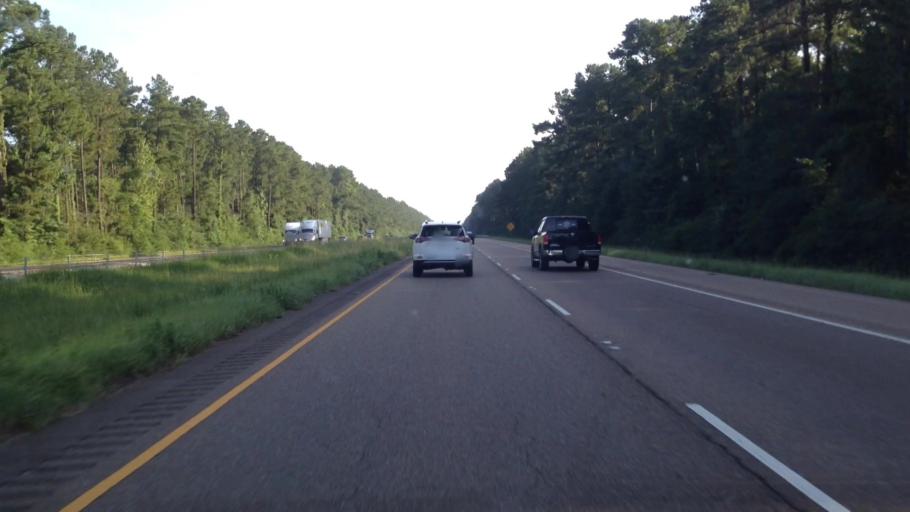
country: US
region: Louisiana
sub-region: Tangipahoa Parish
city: Independence
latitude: 30.6701
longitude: -90.5326
